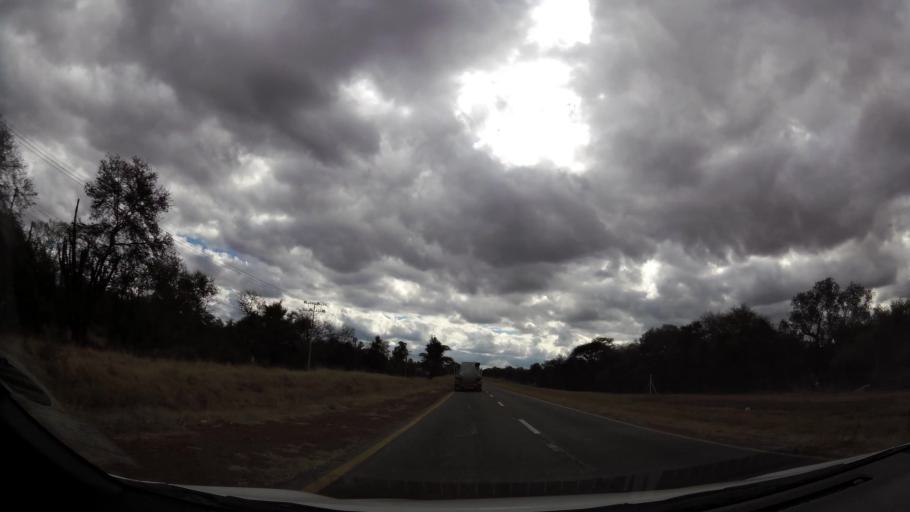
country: ZA
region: Limpopo
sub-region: Waterberg District Municipality
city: Modimolle
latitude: -24.7372
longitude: 28.4353
